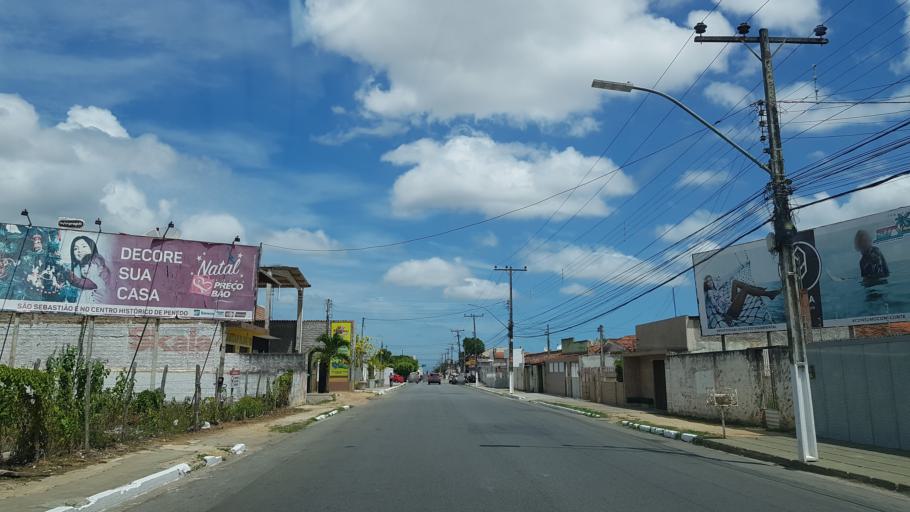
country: BR
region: Alagoas
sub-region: Penedo
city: Penedo
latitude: -10.2836
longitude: -36.5639
